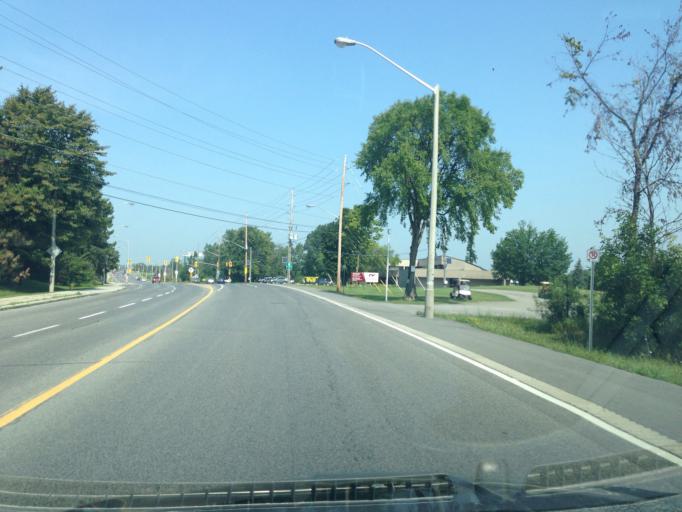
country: CA
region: Ontario
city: Ottawa
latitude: 45.4259
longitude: -75.5992
